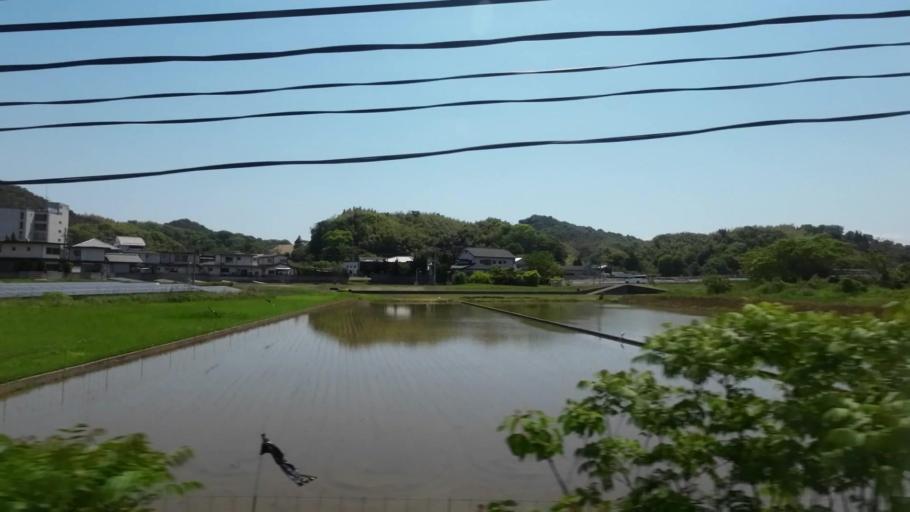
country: JP
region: Ehime
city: Saijo
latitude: 34.0072
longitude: 133.0365
